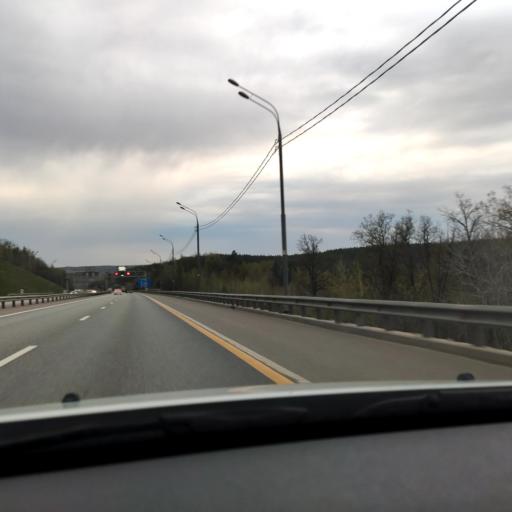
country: RU
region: Lipetsk
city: Zadonsk
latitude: 52.3639
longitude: 38.9312
